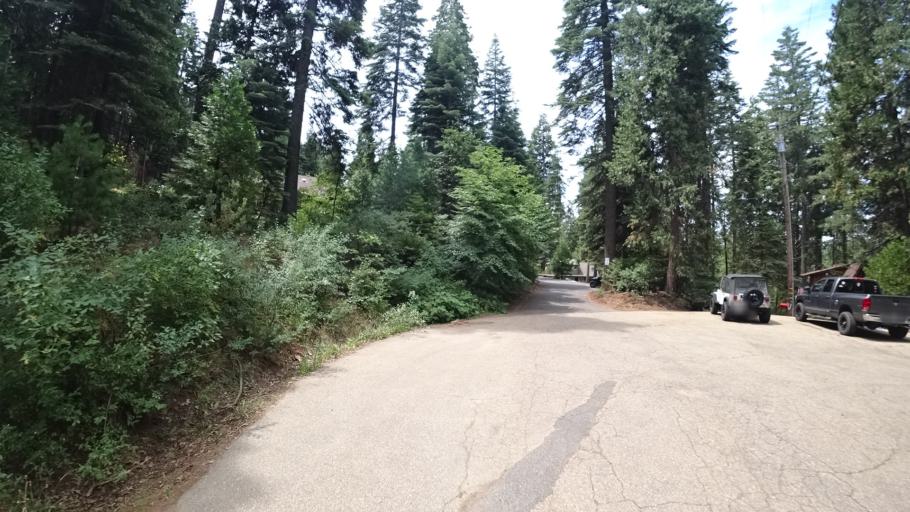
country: US
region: California
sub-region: Calaveras County
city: Arnold
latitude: 38.2515
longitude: -120.3539
